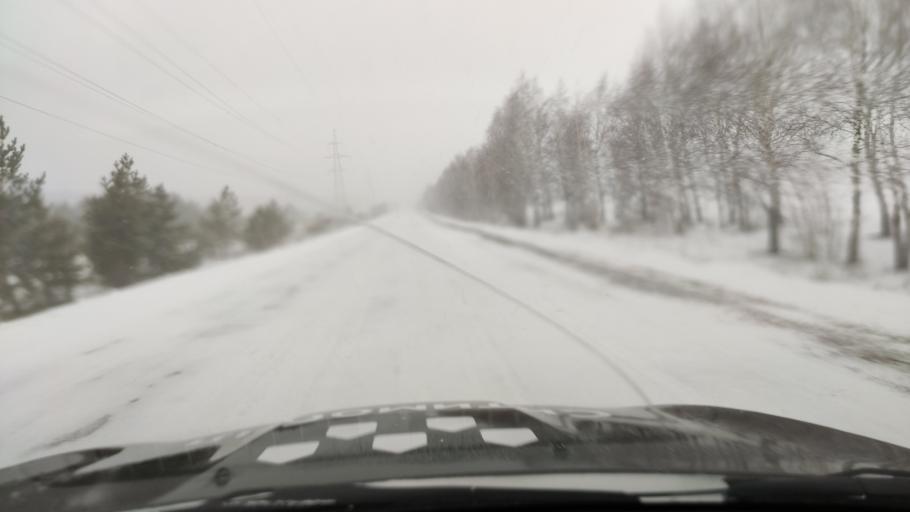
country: RU
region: Samara
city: Povolzhskiy
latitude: 53.5272
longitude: 49.7129
